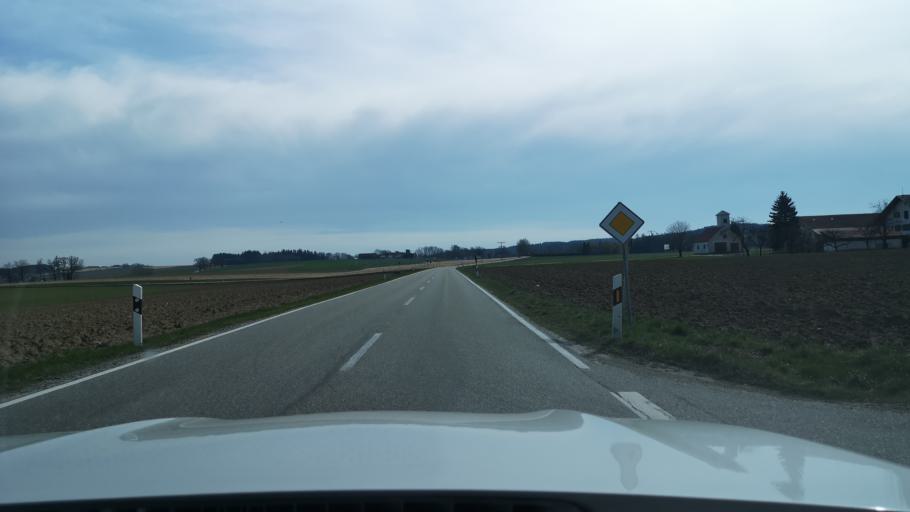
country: DE
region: Bavaria
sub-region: Upper Bavaria
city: Isen
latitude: 48.2018
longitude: 12.0528
